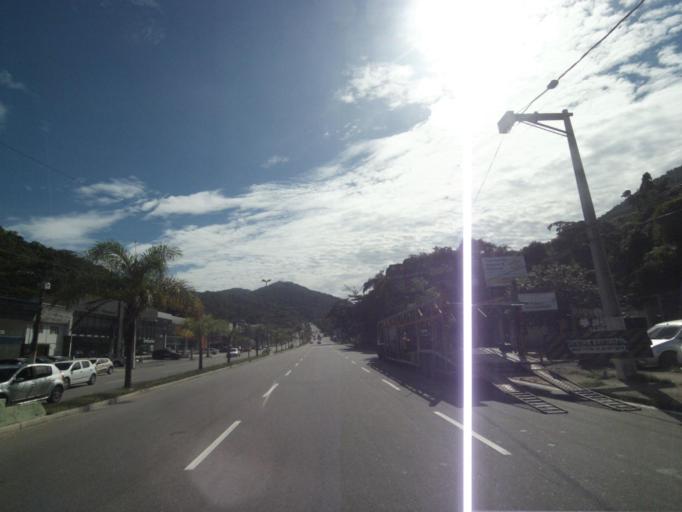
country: BR
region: Rio de Janeiro
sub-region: Niteroi
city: Niteroi
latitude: -22.9300
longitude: -43.0652
